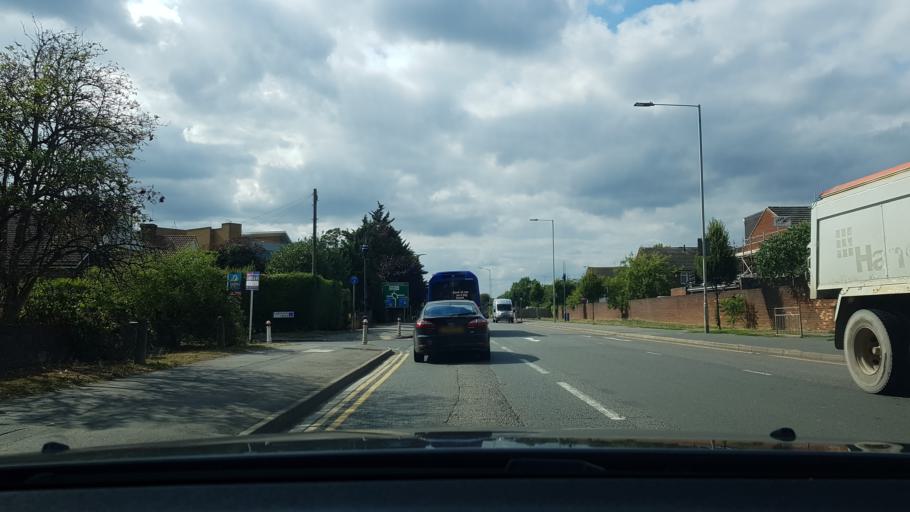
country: GB
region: England
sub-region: Royal Borough of Windsor and Maidenhead
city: Horton
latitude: 51.4901
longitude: -0.5383
